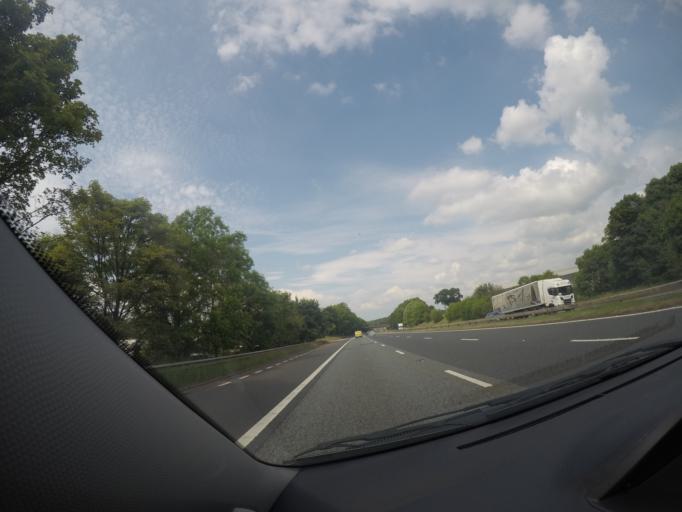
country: GB
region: England
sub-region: Cumbria
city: Scotby
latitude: 54.8414
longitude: -2.8868
